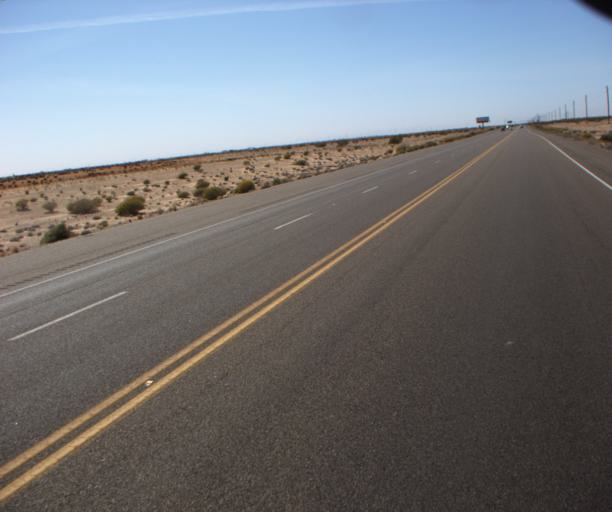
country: MX
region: Sonora
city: San Luis Rio Colorado
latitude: 32.4948
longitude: -114.7046
